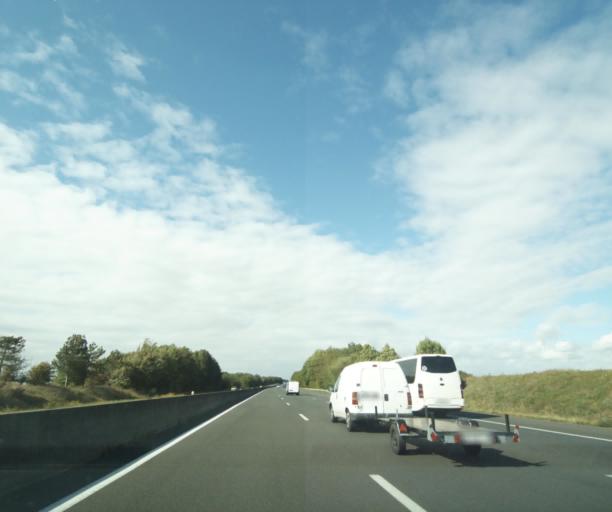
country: FR
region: Centre
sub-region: Departement d'Eure-et-Loir
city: Baigneaux
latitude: 48.1609
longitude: 1.8543
